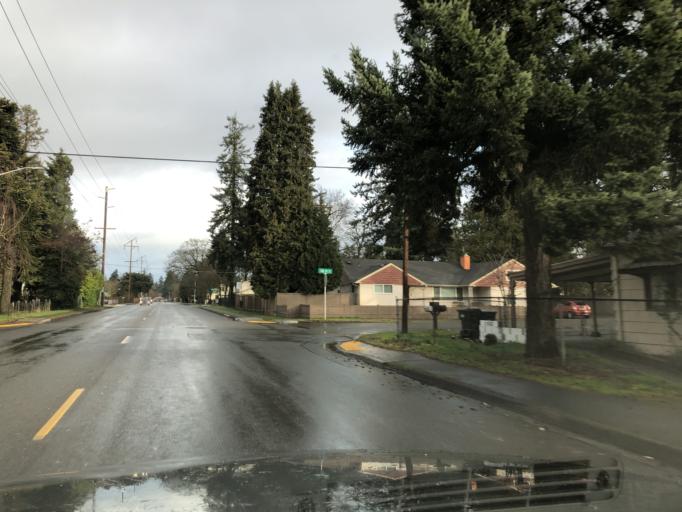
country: US
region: Washington
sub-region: Pierce County
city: Parkland
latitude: 47.1496
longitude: -122.4370
